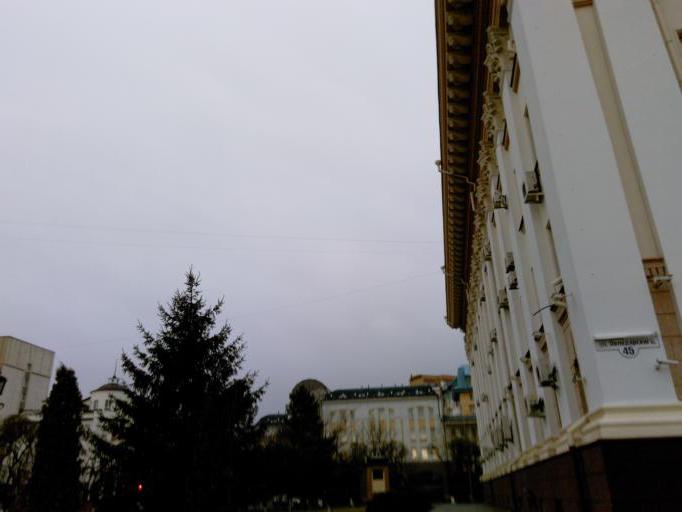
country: RU
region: Tjumen
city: Tyumen
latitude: 57.1543
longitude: 65.5425
